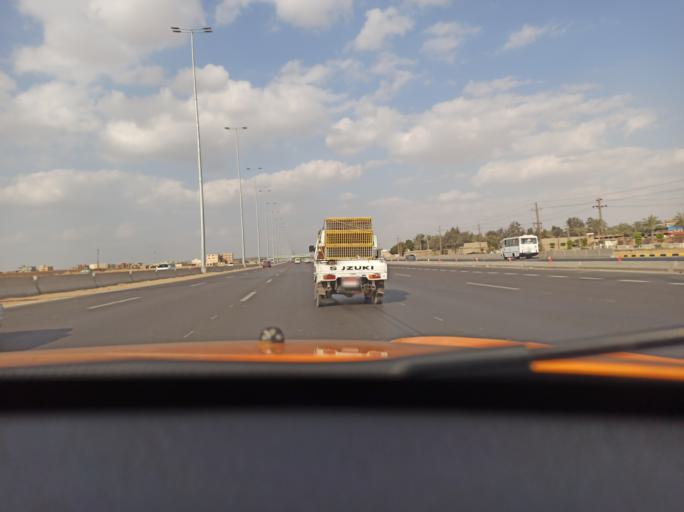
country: EG
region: Eastern Province
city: Bilbays
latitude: 30.2169
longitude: 31.6860
